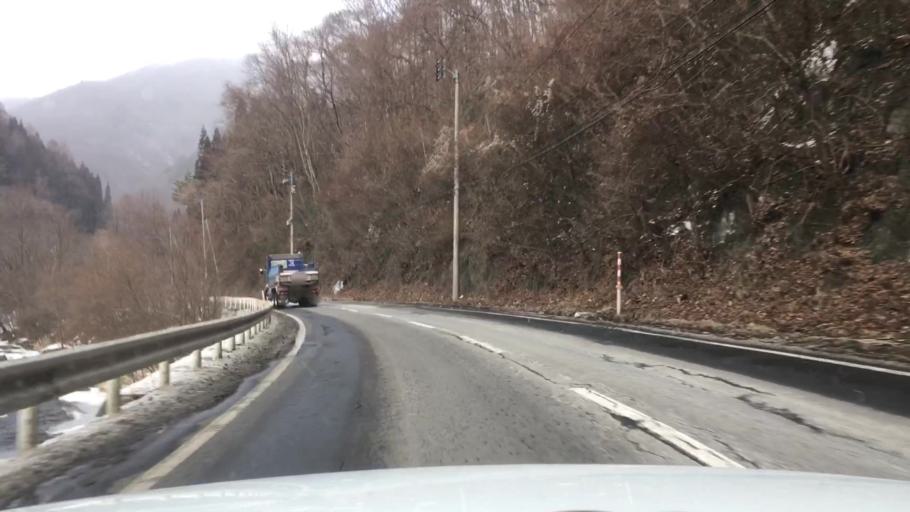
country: JP
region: Iwate
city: Tono
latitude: 39.6180
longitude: 141.4764
